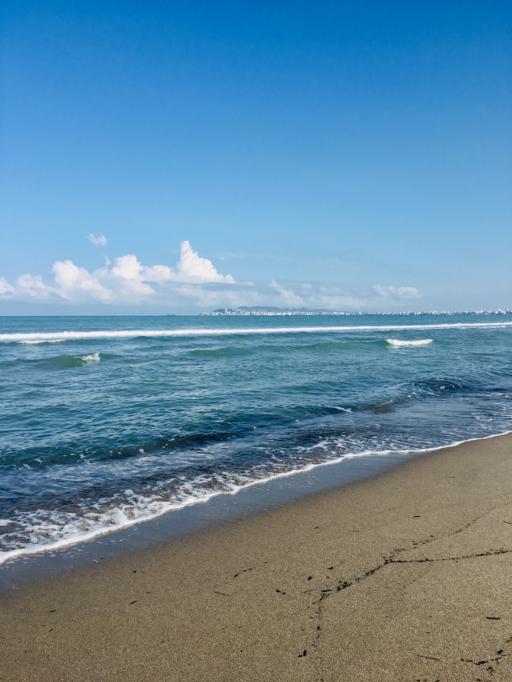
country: AL
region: Tirane
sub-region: Rrethi i Kavajes
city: Golem
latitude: 41.2561
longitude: 19.5192
